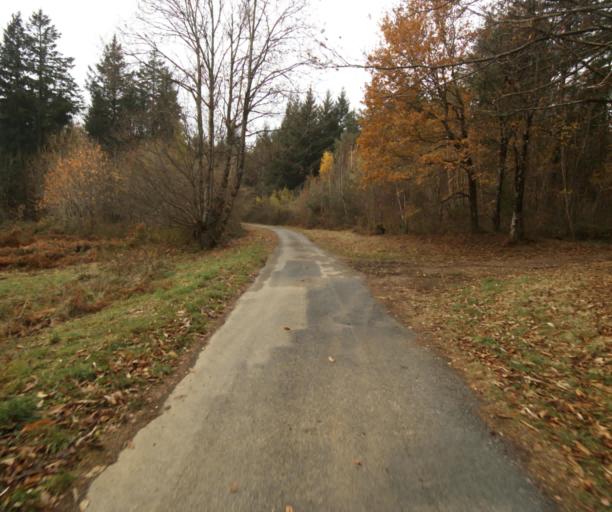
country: FR
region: Limousin
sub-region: Departement de la Correze
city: Sainte-Fortunade
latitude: 45.1931
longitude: 1.7602
